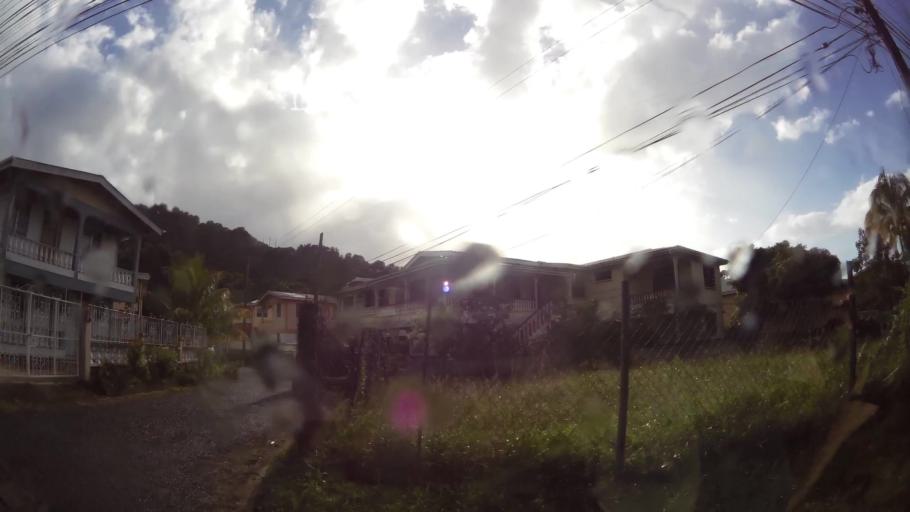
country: DM
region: Saint George
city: Roseau
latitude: 15.3294
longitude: -61.3882
